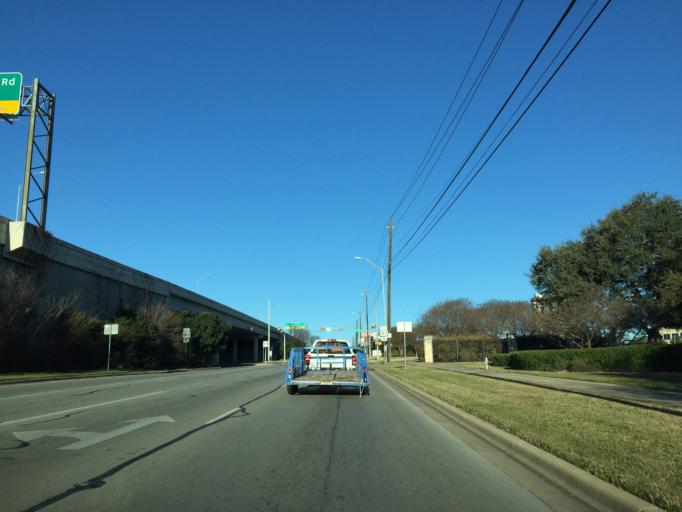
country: US
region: Texas
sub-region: Williamson County
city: Jollyville
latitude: 30.4290
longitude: -97.7580
